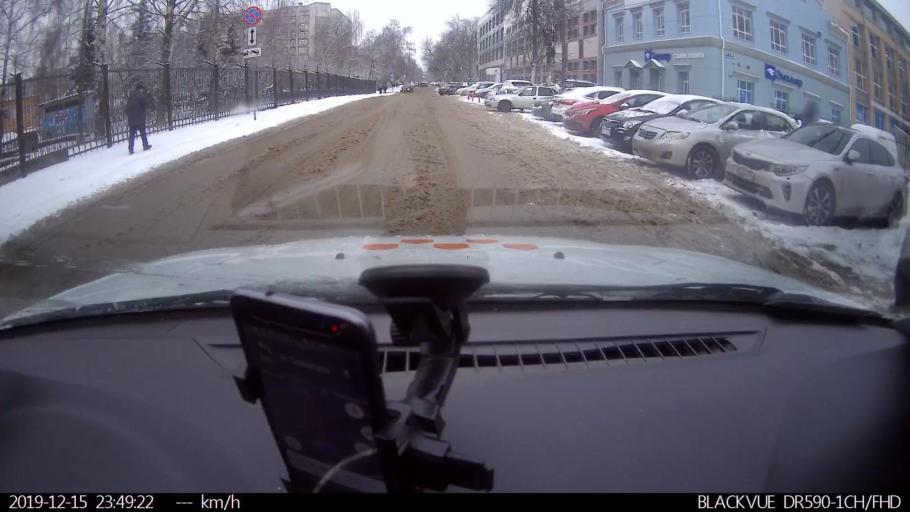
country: RU
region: Nizjnij Novgorod
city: Nizhniy Novgorod
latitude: 56.3076
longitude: 43.9903
